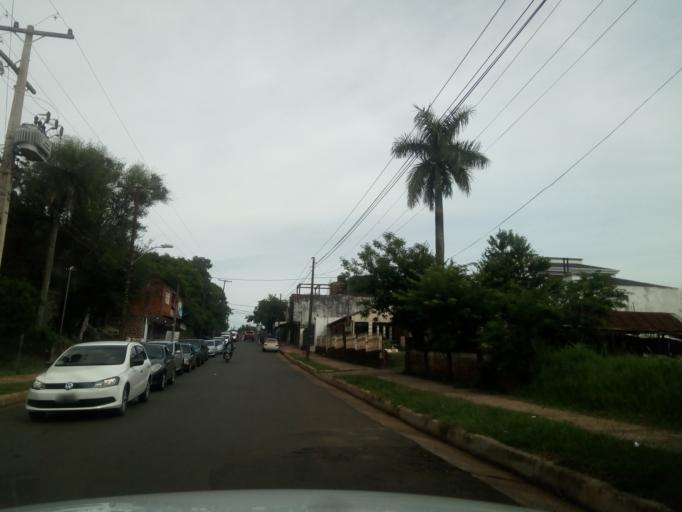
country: PY
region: Itapua
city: Encarnacion
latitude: -27.3587
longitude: -55.8525
